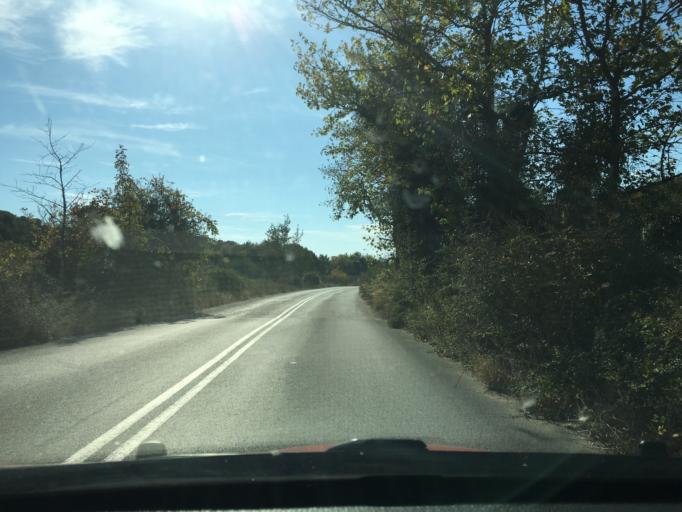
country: GR
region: Central Macedonia
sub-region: Nomos Chalkidikis
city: Megali Panagia
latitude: 40.3842
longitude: 23.7072
